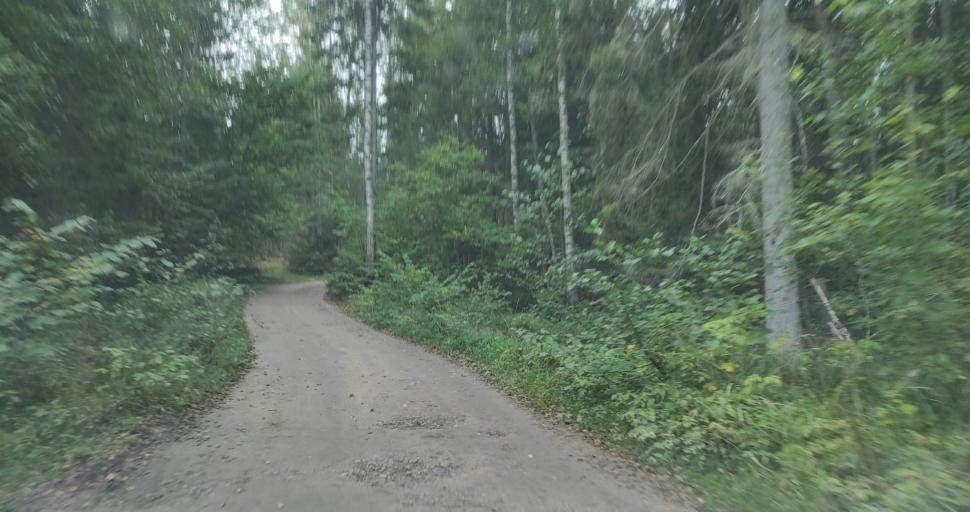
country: LV
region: Kuldigas Rajons
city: Kuldiga
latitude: 57.2387
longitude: 22.0959
